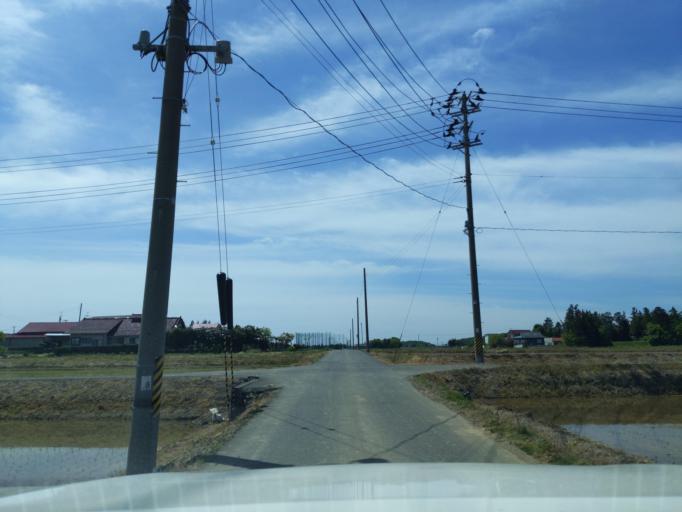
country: JP
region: Fukushima
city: Koriyama
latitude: 37.4131
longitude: 140.3147
